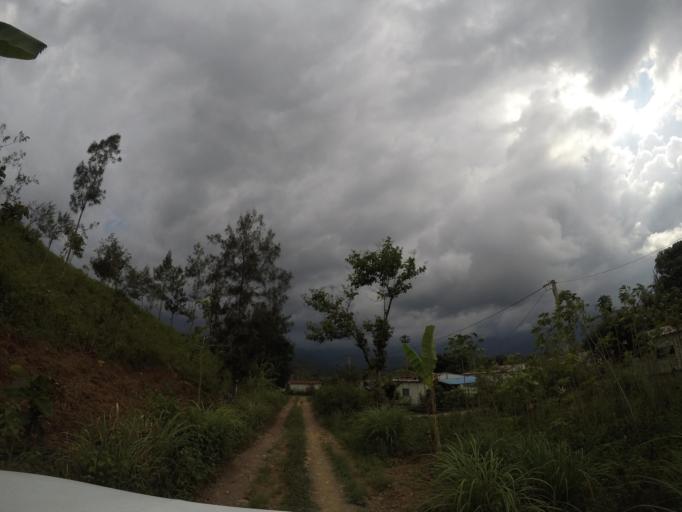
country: TL
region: Ermera
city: Gleno
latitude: -8.7083
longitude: 125.4518
